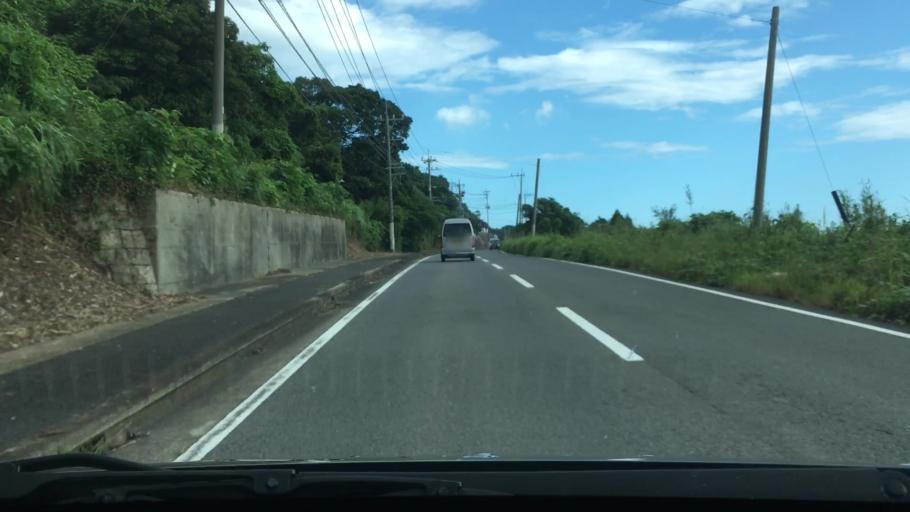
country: JP
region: Nagasaki
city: Togitsu
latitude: 32.8654
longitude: 129.6827
